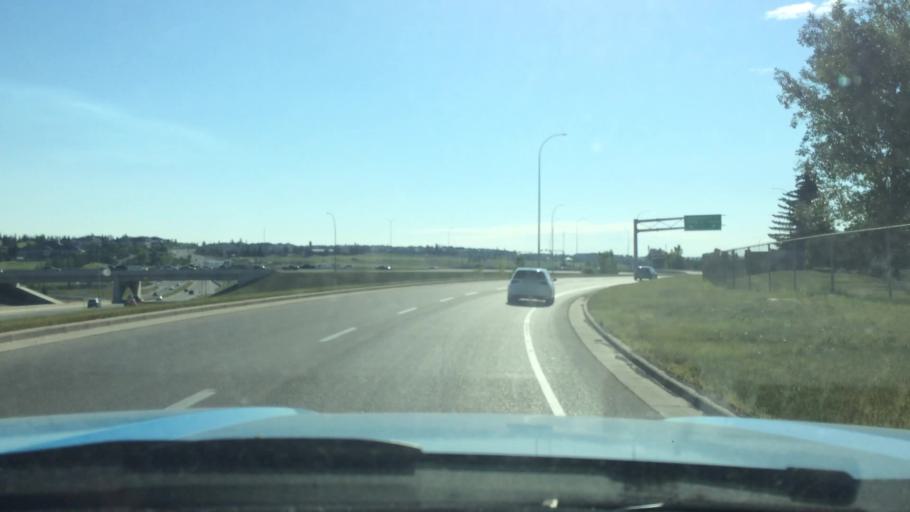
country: CA
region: Alberta
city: Calgary
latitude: 51.1428
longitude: -114.0958
